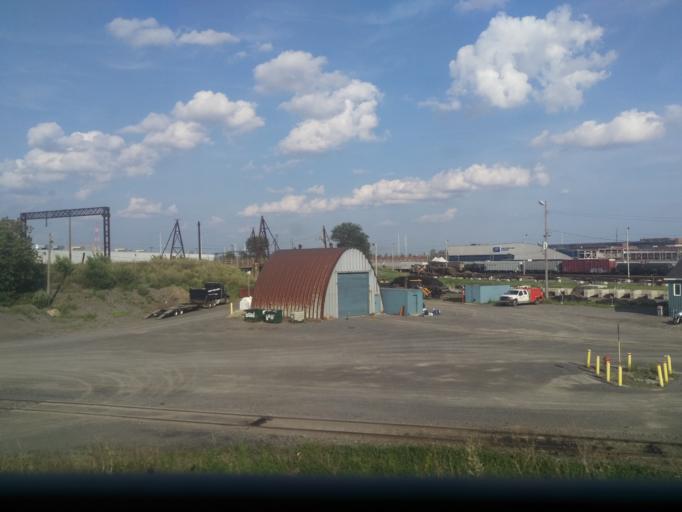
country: CA
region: Quebec
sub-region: Montreal
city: Montreal
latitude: 45.4849
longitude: -73.5559
